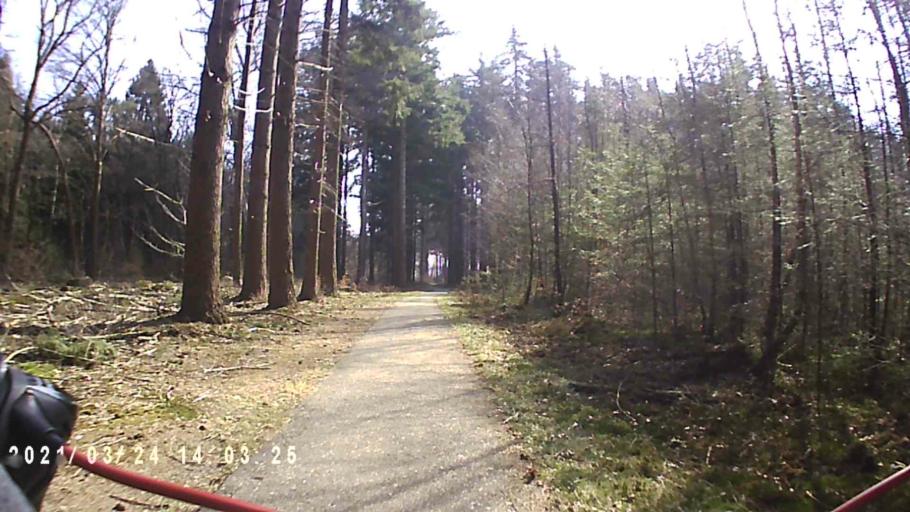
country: NL
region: Friesland
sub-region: Gemeente Smallingerland
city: Drachtstercompagnie
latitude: 53.0799
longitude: 6.2388
